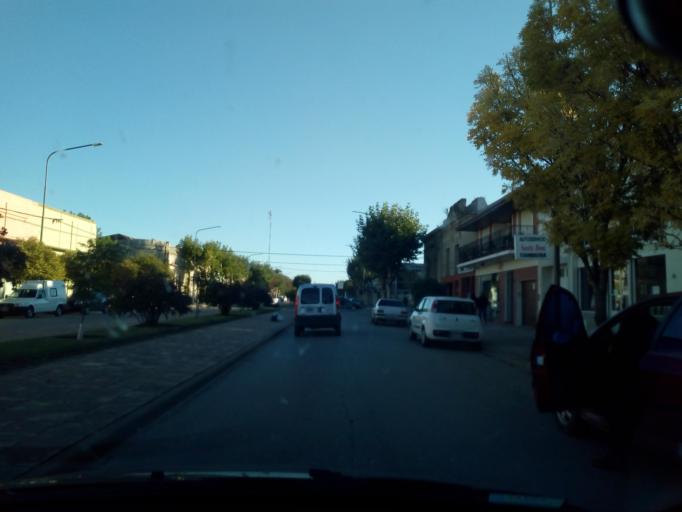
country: AR
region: Buenos Aires
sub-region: Partido de Loberia
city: Loberia
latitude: -38.1613
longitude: -58.7804
